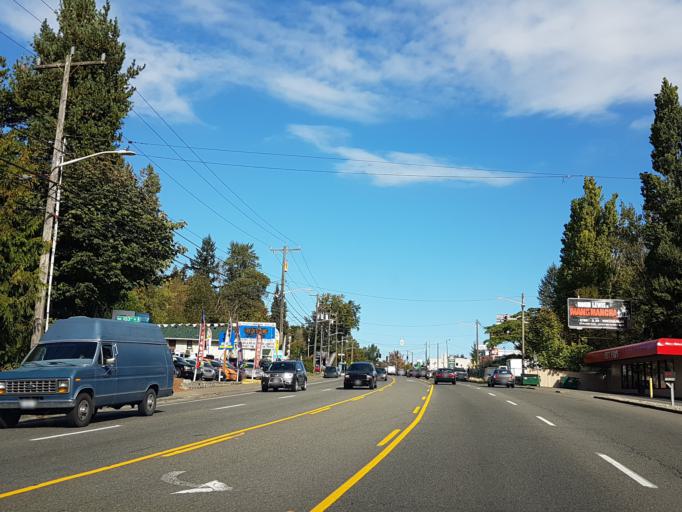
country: US
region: Washington
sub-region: King County
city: Lake Forest Park
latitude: 47.7027
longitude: -122.3016
